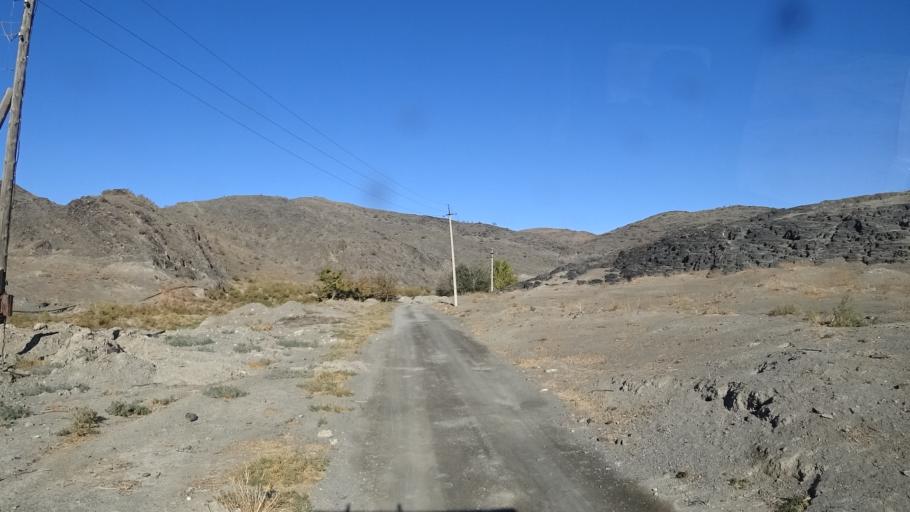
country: UZ
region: Navoiy
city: Nurota
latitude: 40.2977
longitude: 65.6059
